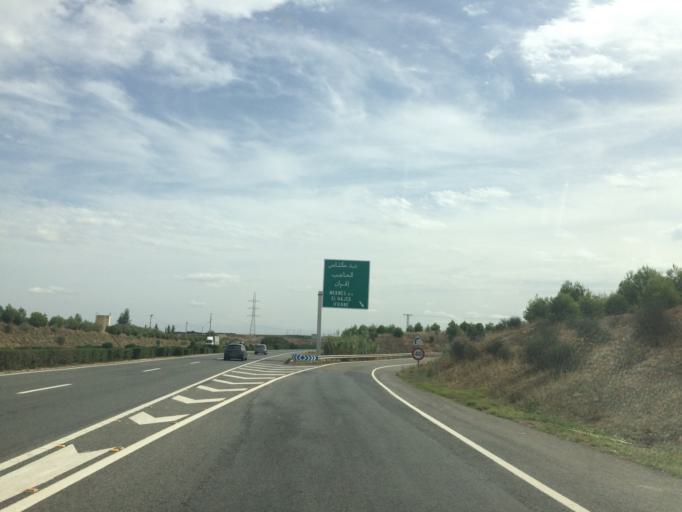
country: MA
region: Meknes-Tafilalet
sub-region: Meknes
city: Meknes
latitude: 33.8304
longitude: -5.5133
